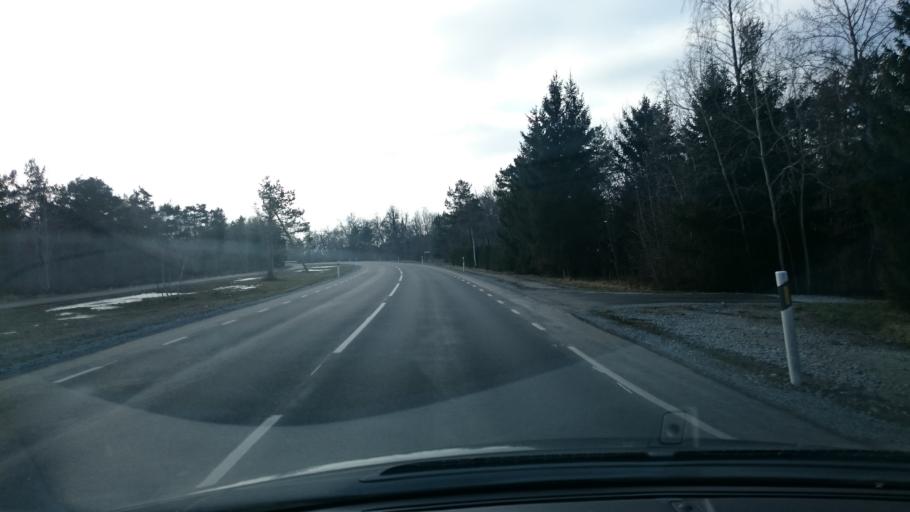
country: EE
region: Harju
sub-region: Paldiski linn
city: Paldiski
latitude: 59.3855
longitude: 24.2366
